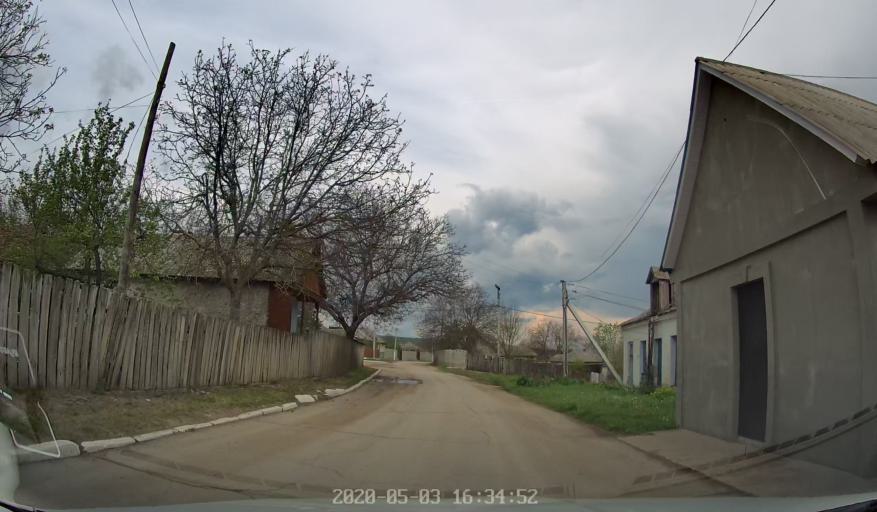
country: MD
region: Calarasi
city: Calarasi
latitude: 47.1908
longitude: 28.3508
